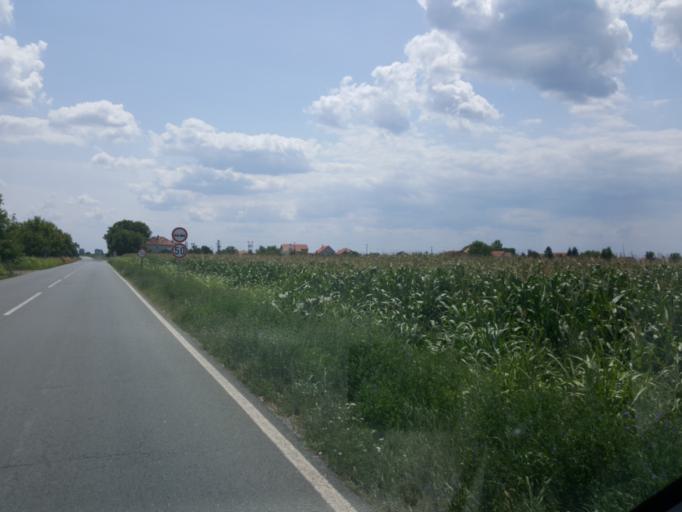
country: RS
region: Autonomna Pokrajina Vojvodina
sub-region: Sremski Okrug
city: Pecinci
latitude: 44.9104
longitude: 19.9565
